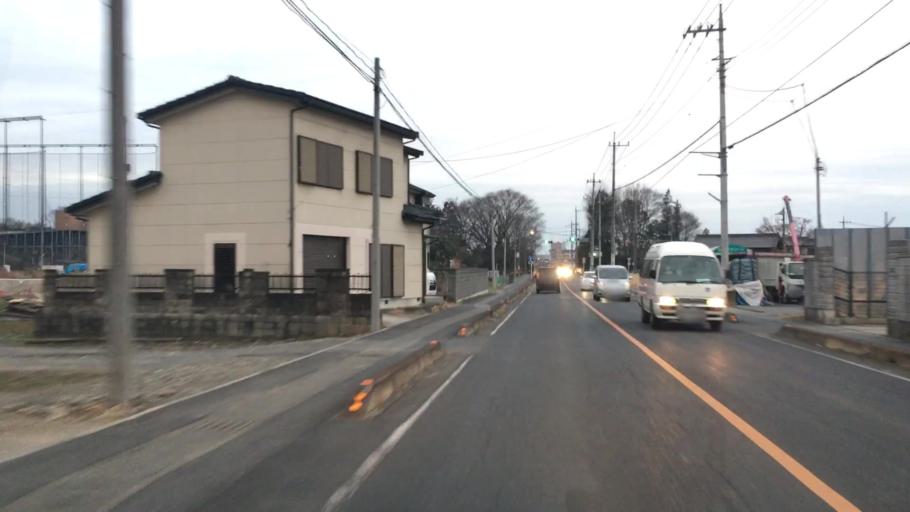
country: JP
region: Gunma
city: Ota
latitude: 36.3084
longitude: 139.3603
